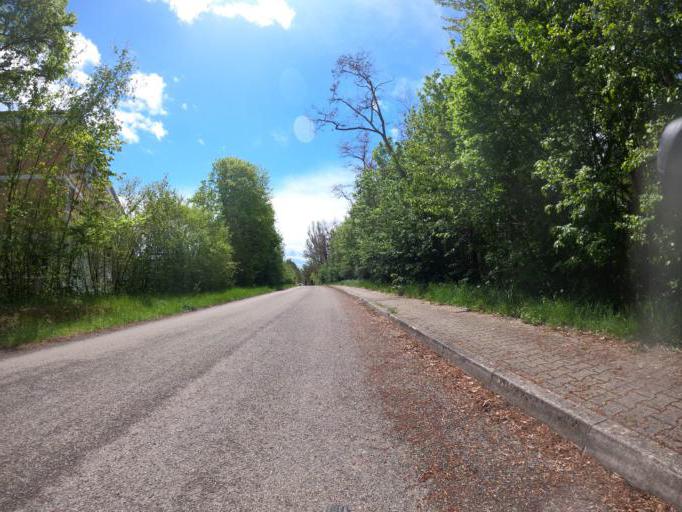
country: DE
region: Baden-Wuerttemberg
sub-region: Karlsruhe Region
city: Nagold
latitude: 48.5620
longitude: 8.7419
